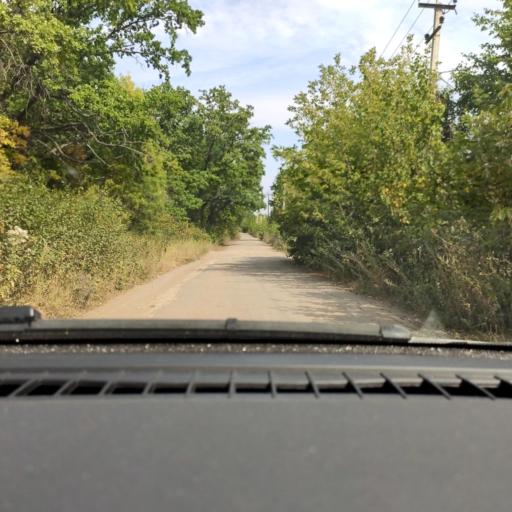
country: RU
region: Voronezj
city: Pridonskoy
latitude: 51.7515
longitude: 39.0772
